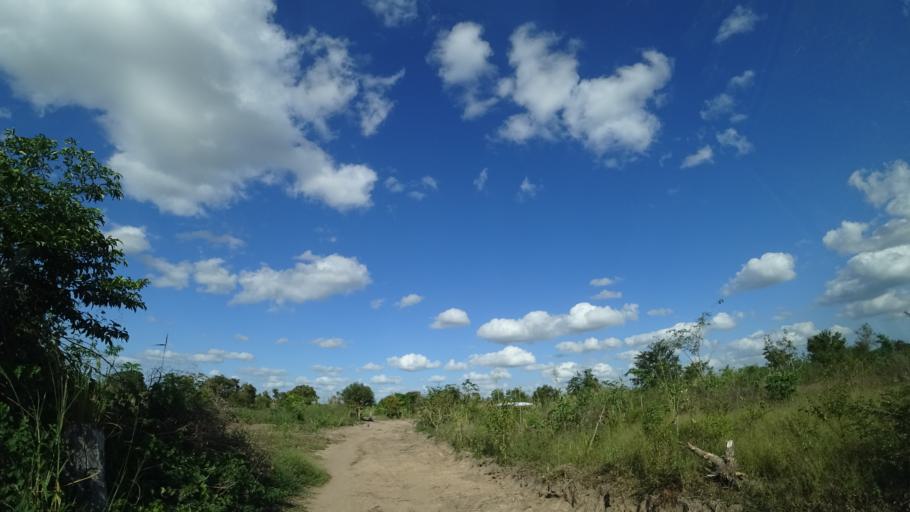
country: MZ
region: Sofala
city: Dondo
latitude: -19.4247
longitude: 34.7213
